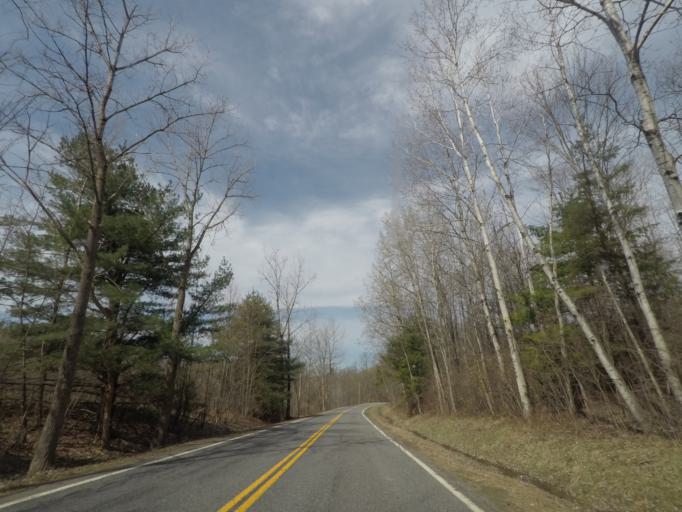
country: US
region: New York
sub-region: Saratoga County
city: Country Knolls
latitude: 42.9074
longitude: -73.7676
